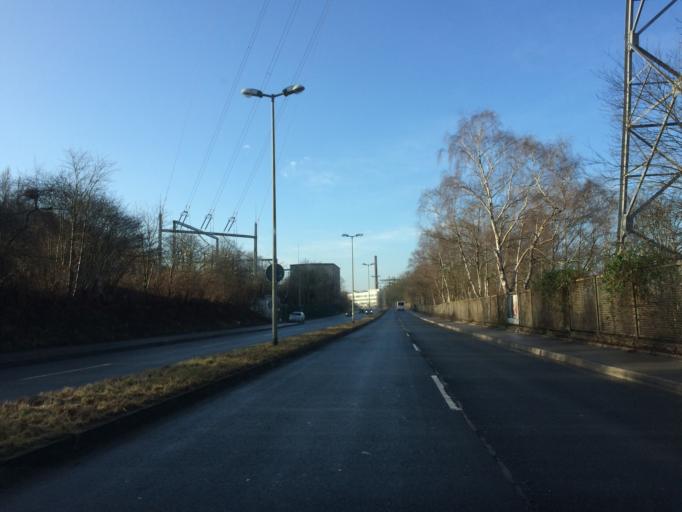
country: DE
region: North Rhine-Westphalia
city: Hattingen
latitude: 51.4126
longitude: 7.1966
